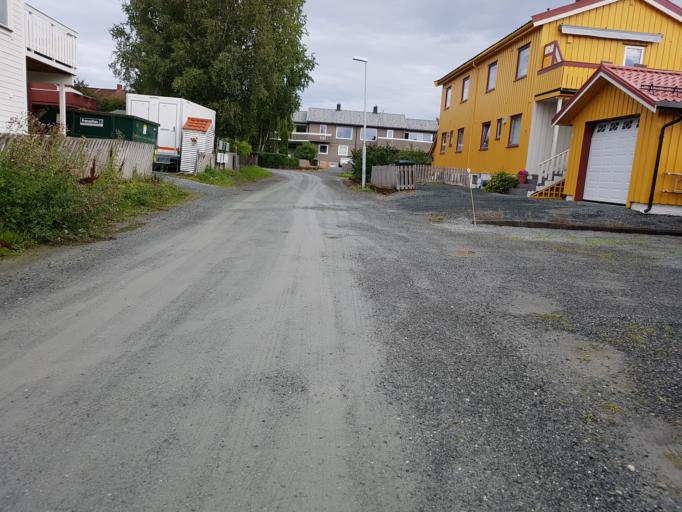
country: NO
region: Sor-Trondelag
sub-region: Trondheim
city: Trondheim
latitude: 63.4041
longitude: 10.4243
